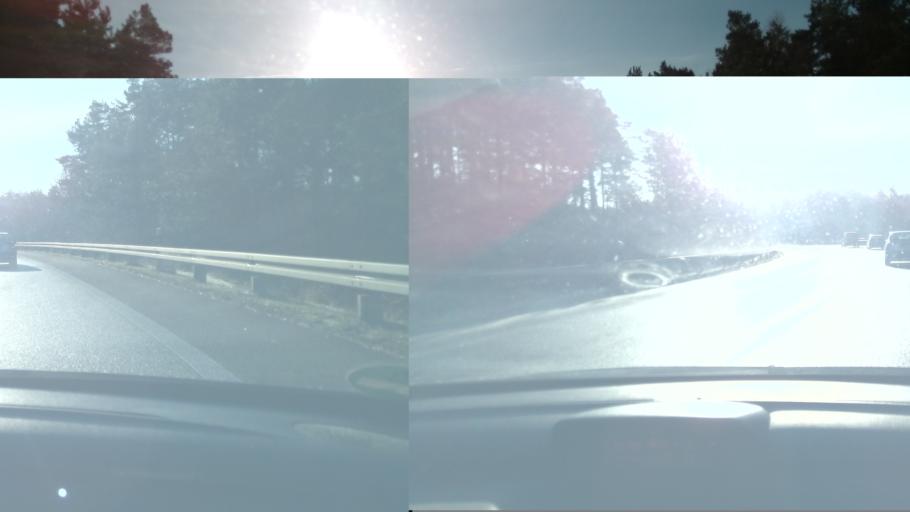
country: DE
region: Mecklenburg-Vorpommern
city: Neustrelitz
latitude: 53.3753
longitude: 13.0773
